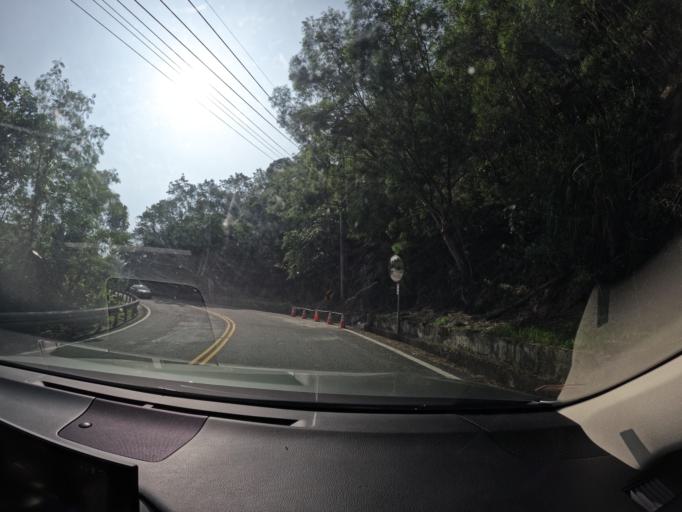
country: TW
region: Taiwan
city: Yujing
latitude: 23.0681
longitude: 120.5533
